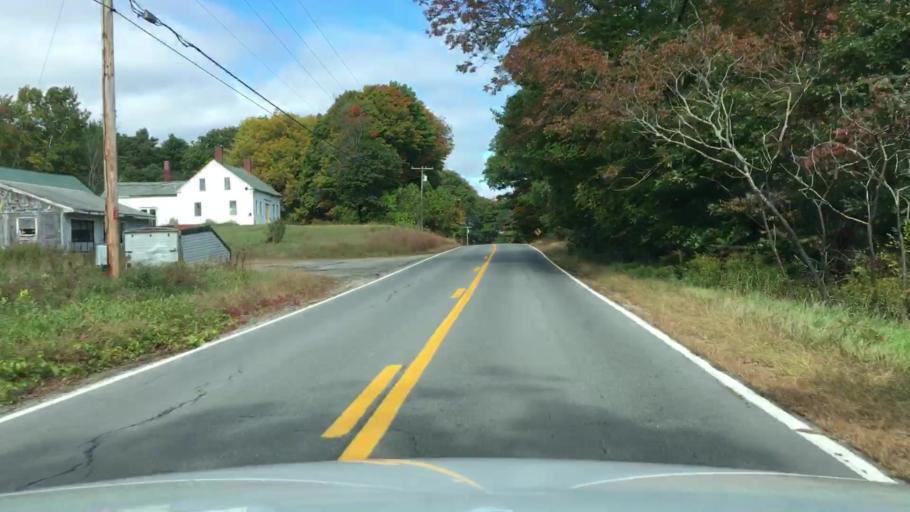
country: US
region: Maine
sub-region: Sagadahoc County
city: North Bath
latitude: 43.9782
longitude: -69.8899
